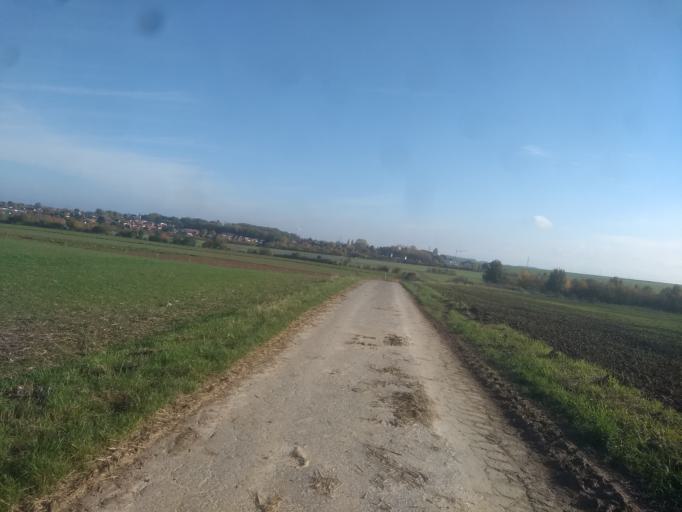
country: FR
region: Nord-Pas-de-Calais
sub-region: Departement du Pas-de-Calais
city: Beaurains
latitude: 50.2767
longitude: 2.8015
